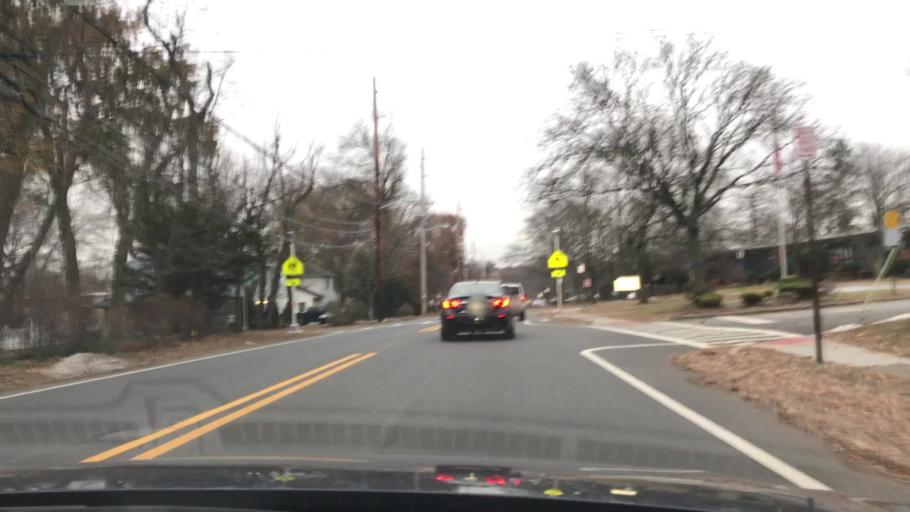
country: US
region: New Jersey
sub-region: Bergen County
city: Ho-Ho-Kus
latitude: 40.9715
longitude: -74.0891
